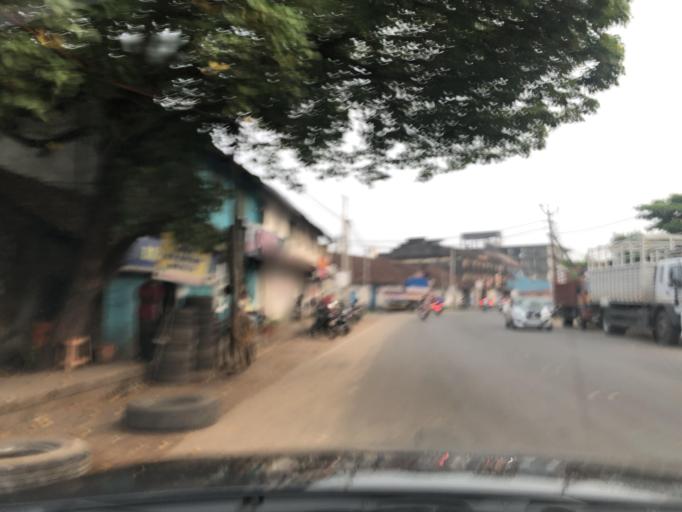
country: IN
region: Kerala
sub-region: Kozhikode
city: Kozhikode
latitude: 11.2501
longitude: 75.7722
